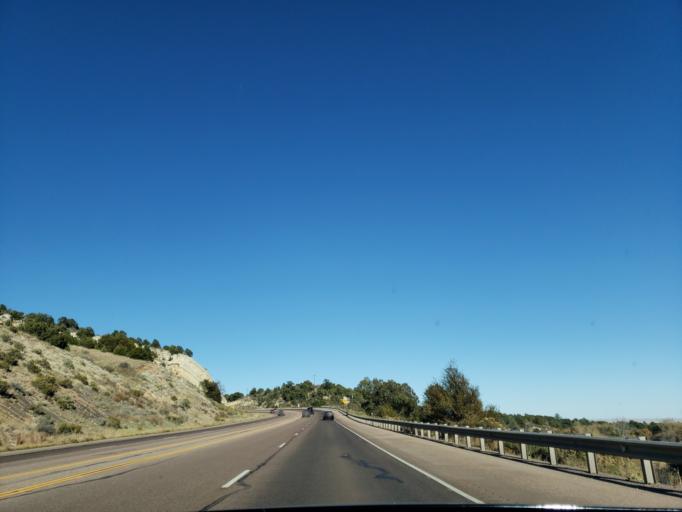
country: US
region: Colorado
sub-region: El Paso County
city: Fort Carson
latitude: 38.6726
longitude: -104.8545
